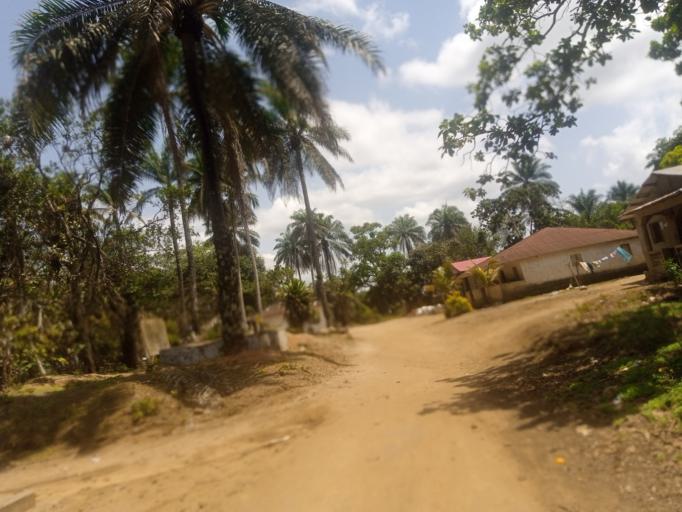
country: SL
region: Western Area
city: Waterloo
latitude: 8.3173
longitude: -13.0054
